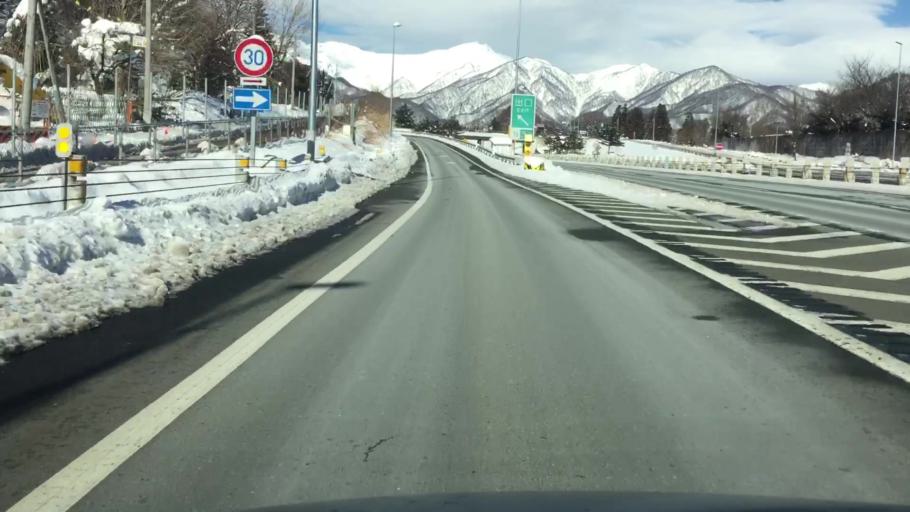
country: JP
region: Gunma
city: Numata
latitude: 36.7443
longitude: 138.9769
